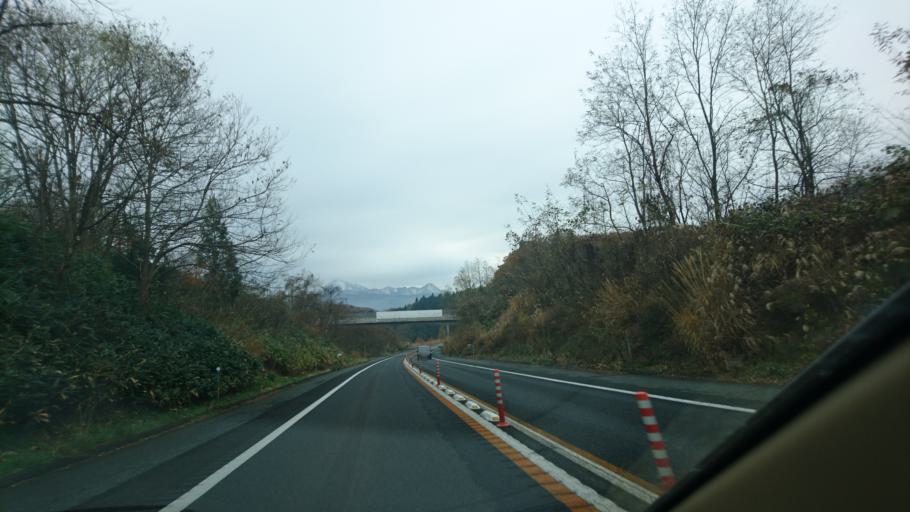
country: JP
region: Iwate
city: Kitakami
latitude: 39.2802
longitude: 141.0223
